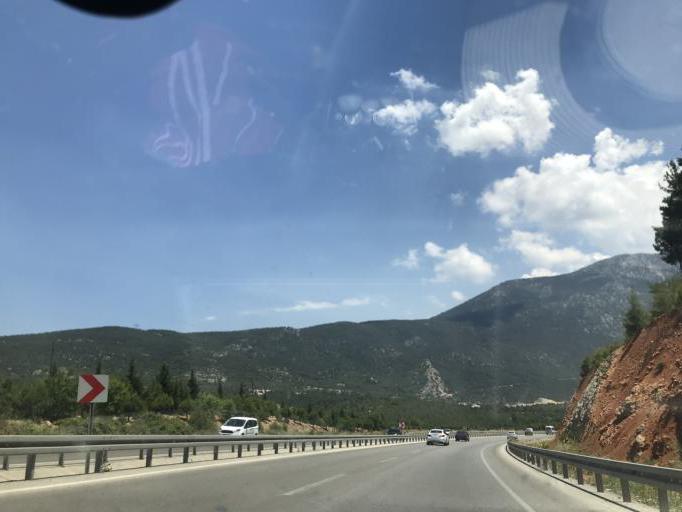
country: TR
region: Denizli
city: Honaz
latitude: 37.7305
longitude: 29.1909
